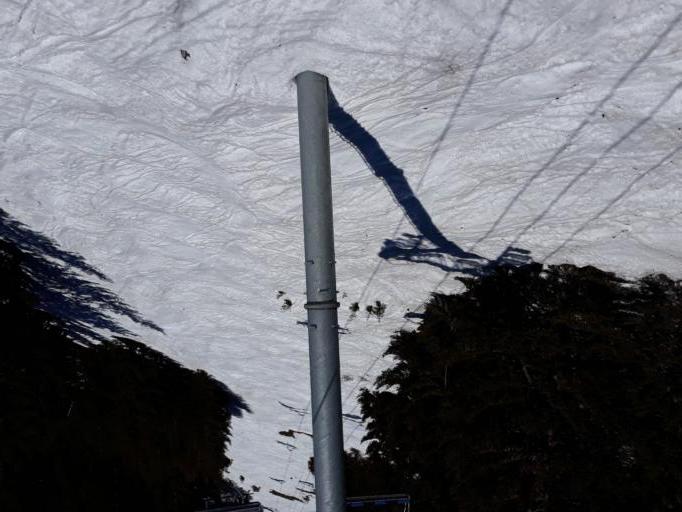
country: FR
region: Rhone-Alpes
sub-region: Departement de la Haute-Savoie
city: Araches-la-Frasse
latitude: 46.0321
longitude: 6.6758
